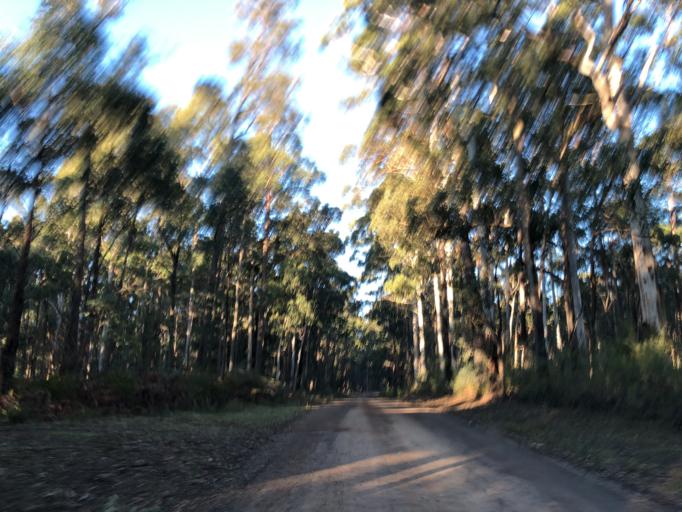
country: AU
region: Victoria
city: Brown Hill
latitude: -37.4735
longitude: 144.1714
